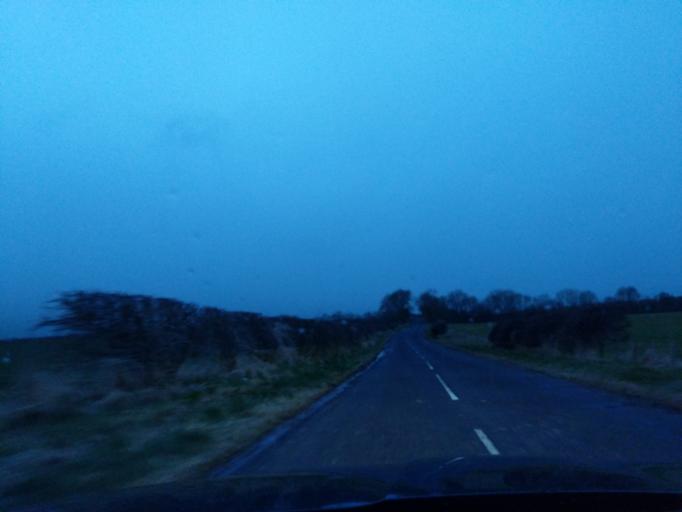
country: GB
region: England
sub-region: Northumberland
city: Ford
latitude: 55.7152
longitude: -2.1323
